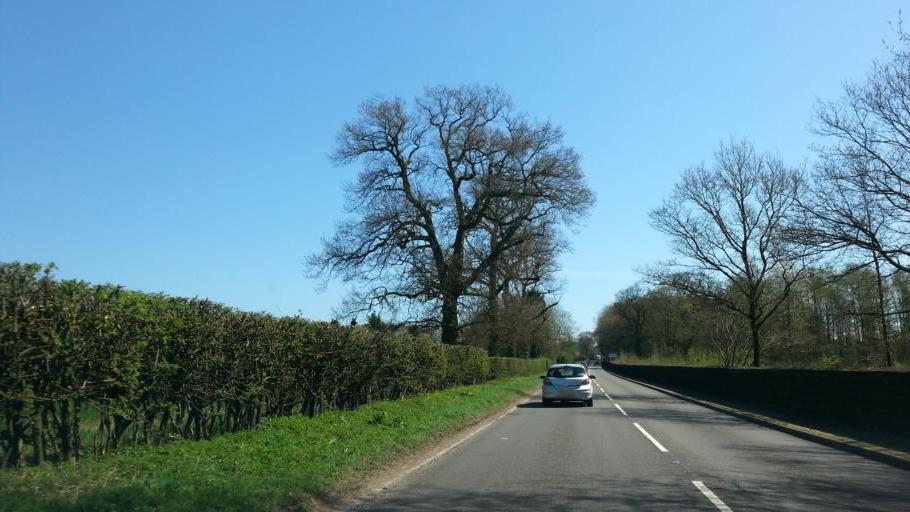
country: GB
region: England
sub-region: Shropshire
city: Tong
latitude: 52.6951
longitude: -2.2817
